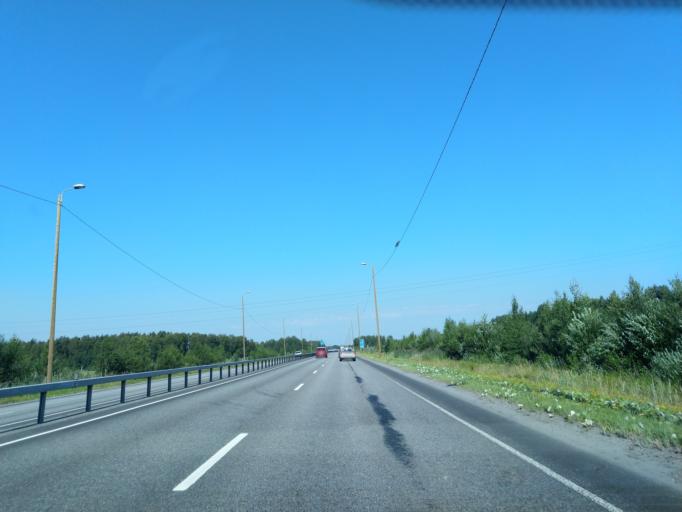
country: FI
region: Satakunta
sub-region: Pori
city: Nakkila
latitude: 61.3400
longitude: 22.0383
